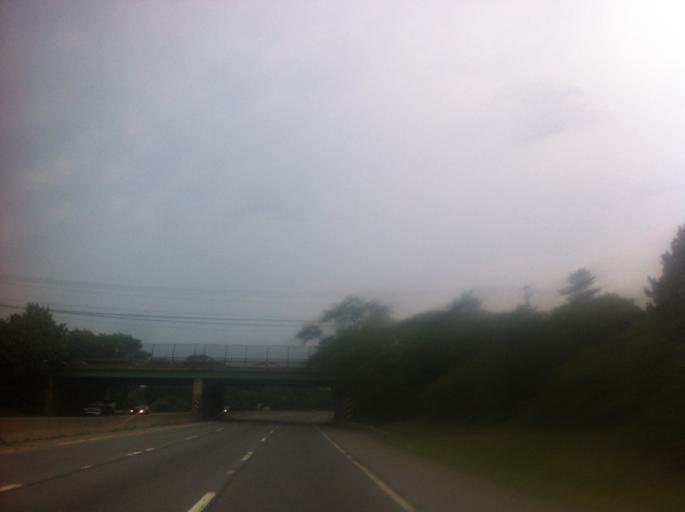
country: US
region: New York
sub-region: Nassau County
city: Plainview
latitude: 40.7679
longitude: -73.4787
